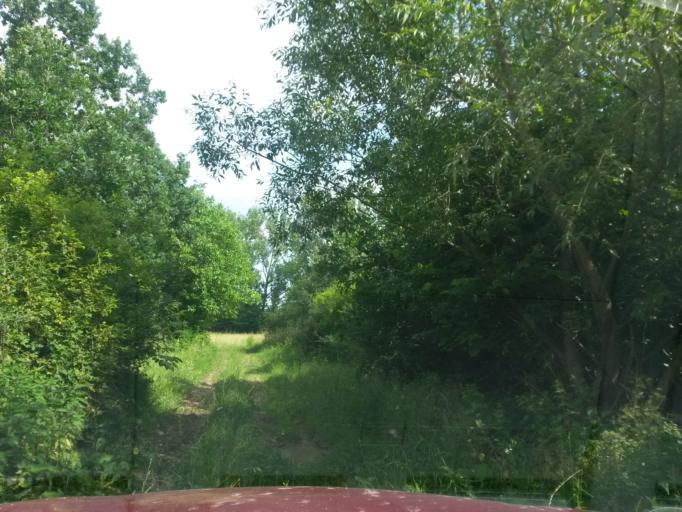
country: SK
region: Kosicky
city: Moldava nad Bodvou
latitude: 48.6206
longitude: 21.0993
